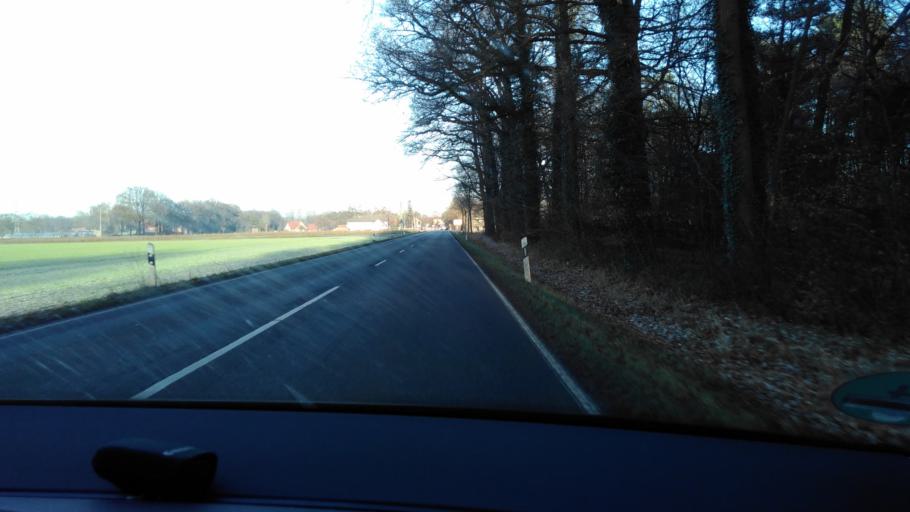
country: DE
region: North Rhine-Westphalia
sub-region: Regierungsbezirk Detmold
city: Verl
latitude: 51.9015
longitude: 8.5465
